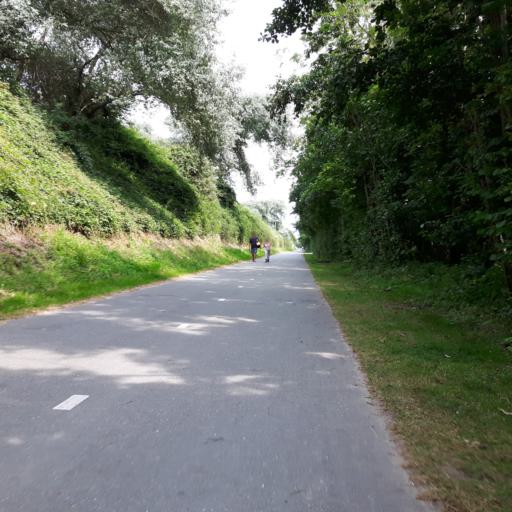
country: NL
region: Zeeland
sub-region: Gemeente Sluis
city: Sluis
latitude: 51.3899
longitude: 3.4491
